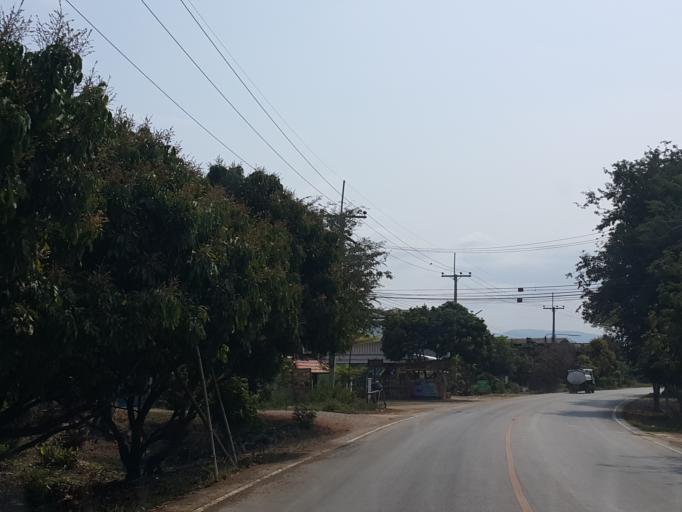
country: TH
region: Lamphun
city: Ban Thi
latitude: 18.6593
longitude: 99.1107
